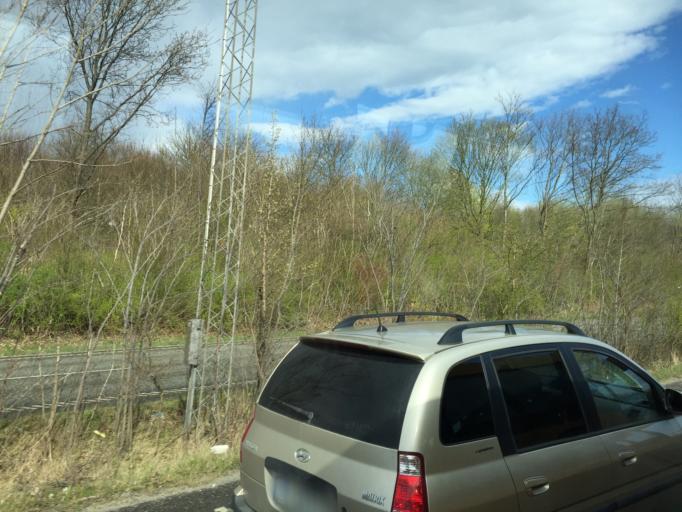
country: SE
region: Skane
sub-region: Lunds Kommun
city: Lund
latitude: 55.6946
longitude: 13.2327
